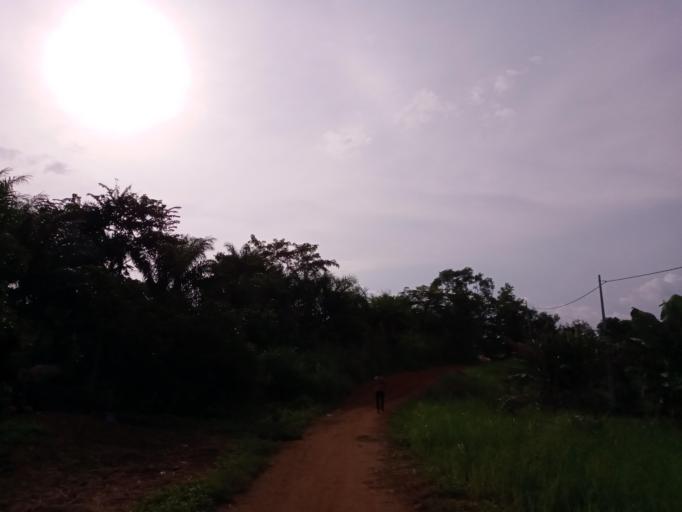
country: SL
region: Northern Province
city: Bumbuna
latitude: 9.0459
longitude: -11.7581
